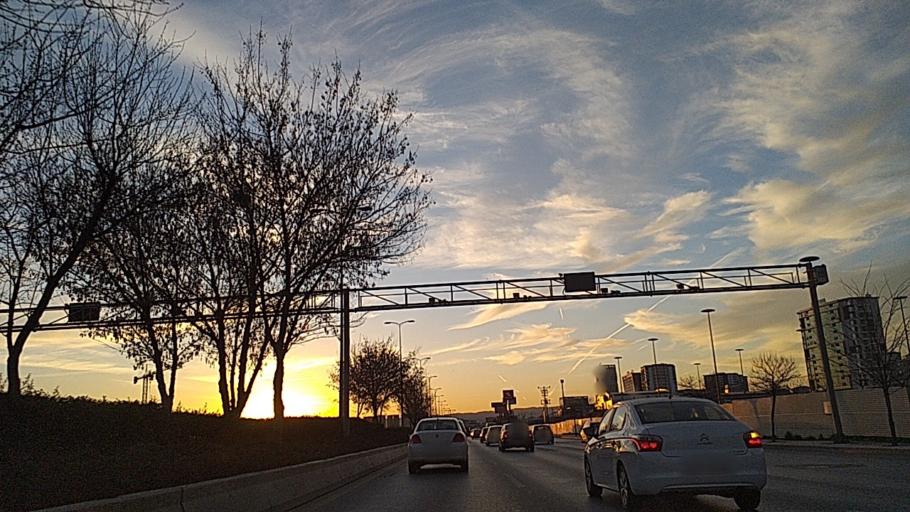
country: TR
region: Ankara
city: Etimesgut
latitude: 39.9636
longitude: 32.6499
